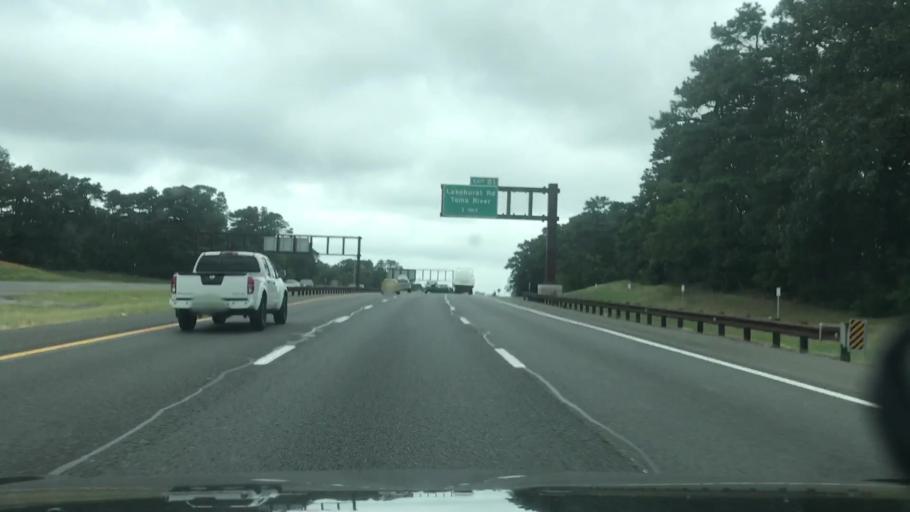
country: US
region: New Jersey
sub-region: Ocean County
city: South Toms River
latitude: 39.9393
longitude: -74.2090
